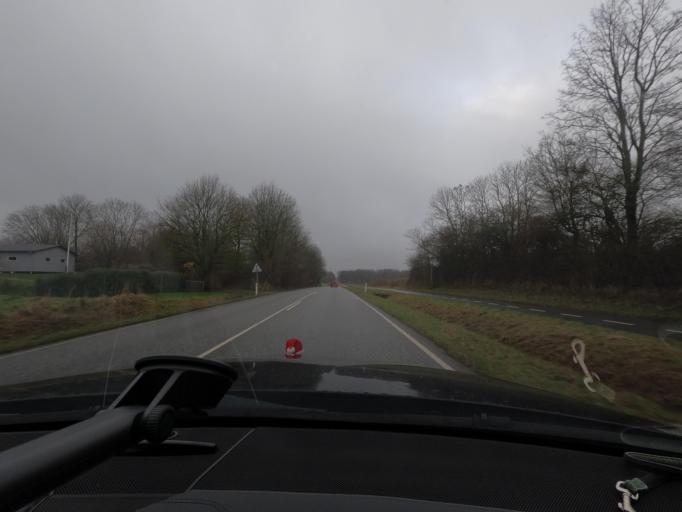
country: DK
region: South Denmark
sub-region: Sonderborg Kommune
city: Sonderborg
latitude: 54.9064
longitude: 9.8480
